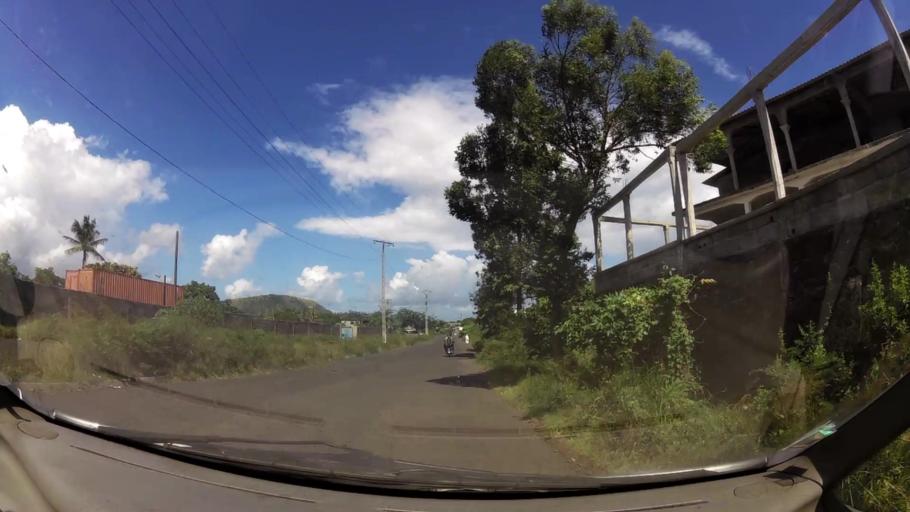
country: KM
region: Grande Comore
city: Mavingouni
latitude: -11.7392
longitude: 43.2403
